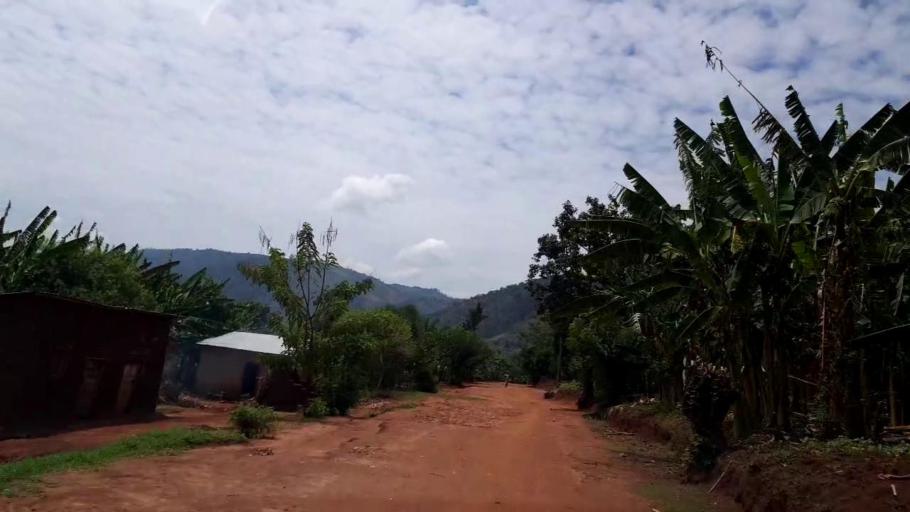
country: RW
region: Northern Province
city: Byumba
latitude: -1.4946
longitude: 30.1952
